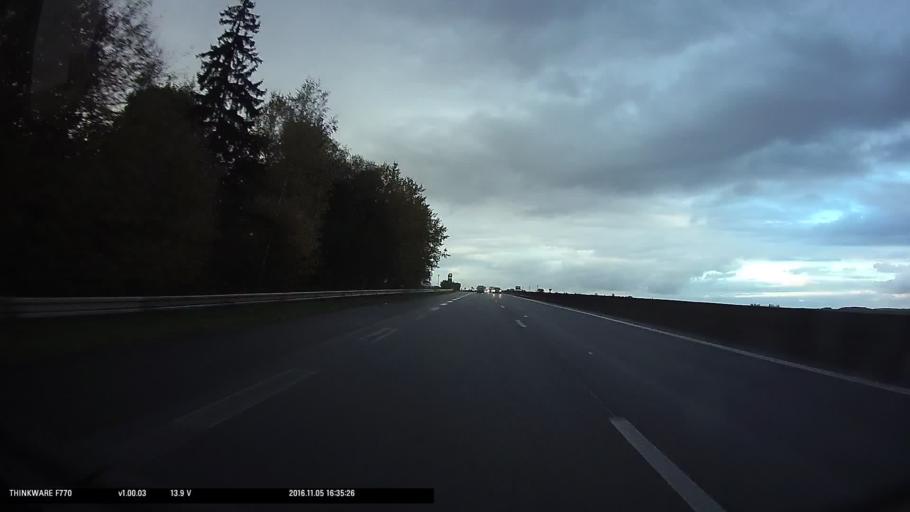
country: FR
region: Ile-de-France
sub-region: Departement du Val-d'Oise
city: Ableiges
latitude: 49.0642
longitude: 1.9815
